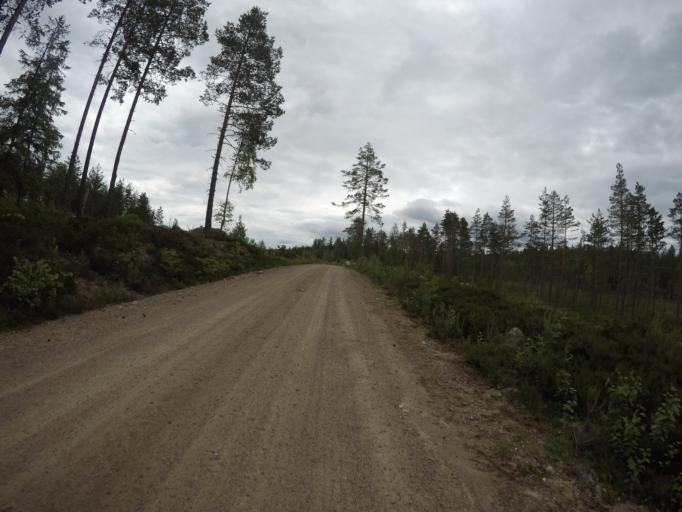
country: SE
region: Dalarna
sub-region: Ludvika Kommun
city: Abborrberget
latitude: 60.0851
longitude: 14.5529
